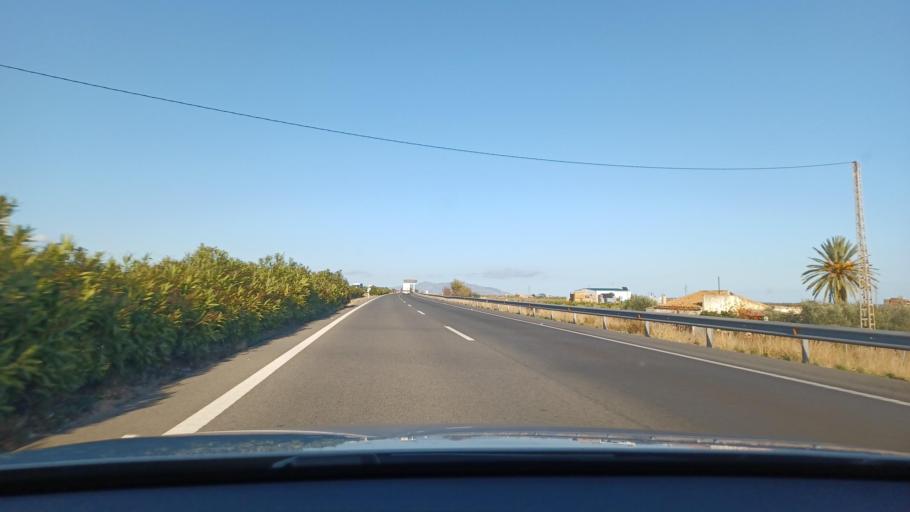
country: ES
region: Valencia
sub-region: Provincia de Castello
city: Orpesa/Oropesa del Mar
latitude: 40.1542
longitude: 0.1500
